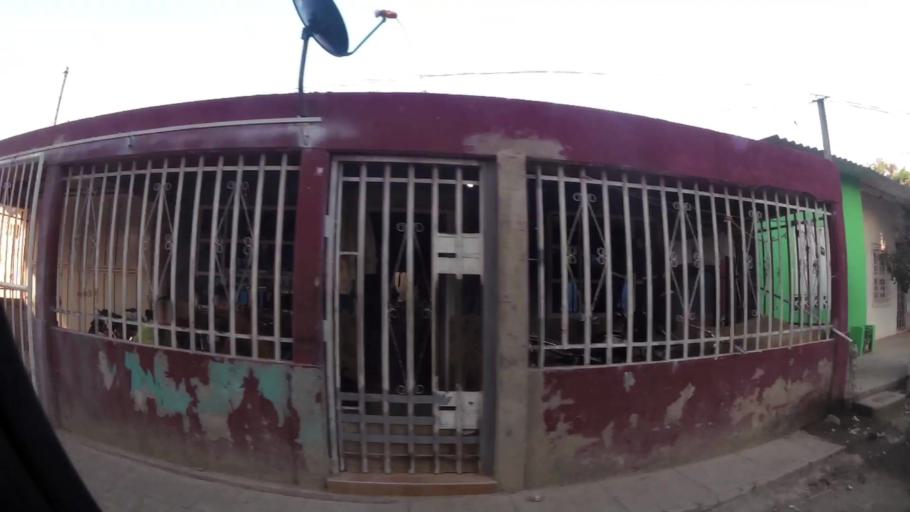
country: CO
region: Bolivar
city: Cartagena
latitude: 10.4109
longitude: -75.4558
